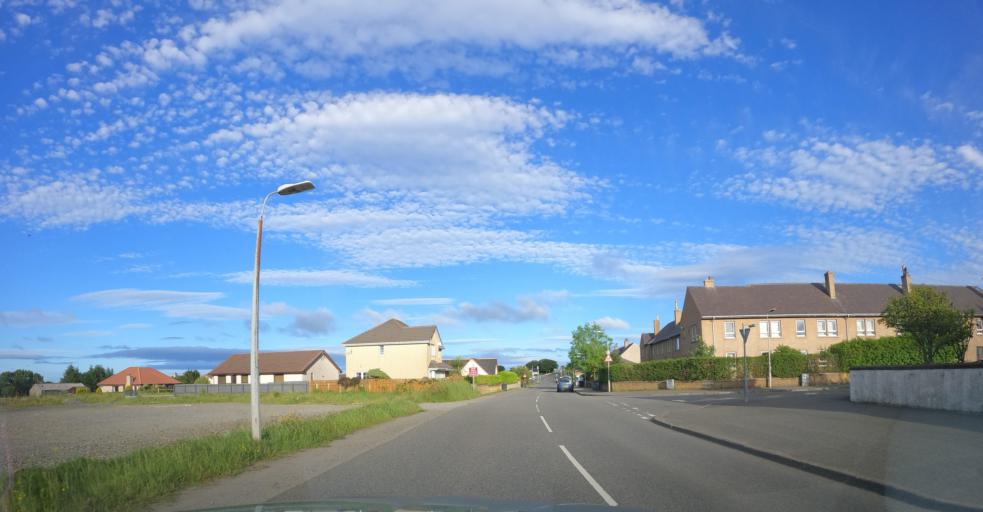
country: GB
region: Scotland
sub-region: Eilean Siar
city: Isle of Lewis
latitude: 58.2179
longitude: -6.3774
